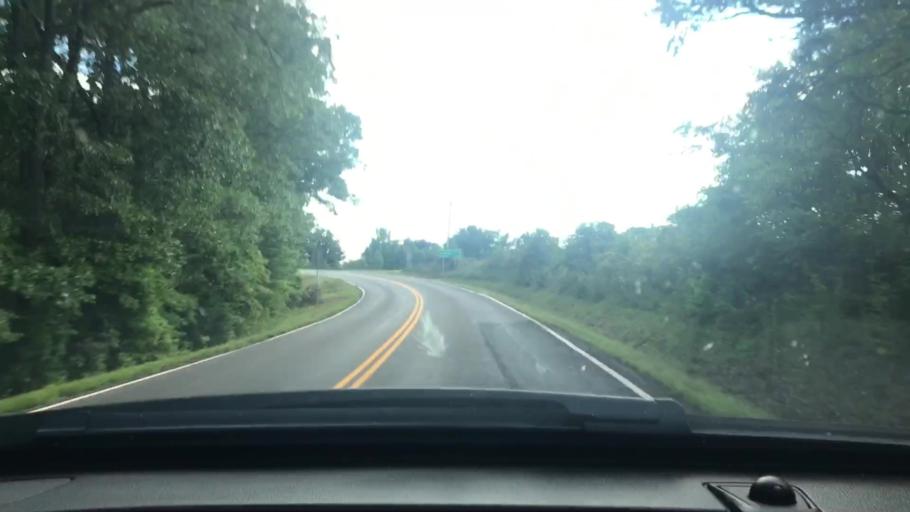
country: US
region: Missouri
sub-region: Wright County
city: Mountain Grove
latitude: 37.3022
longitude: -92.3128
